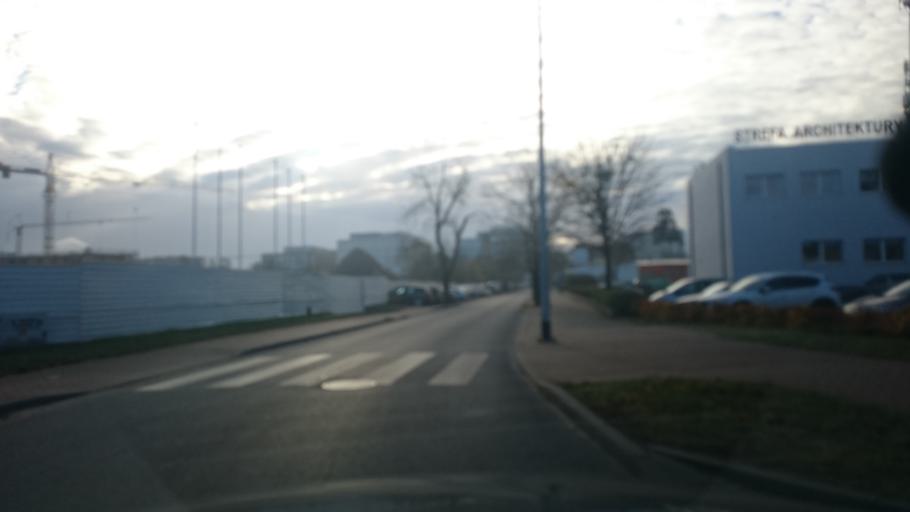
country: PL
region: Pomeranian Voivodeship
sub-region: Sopot
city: Sopot
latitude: 54.4080
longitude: 18.5746
